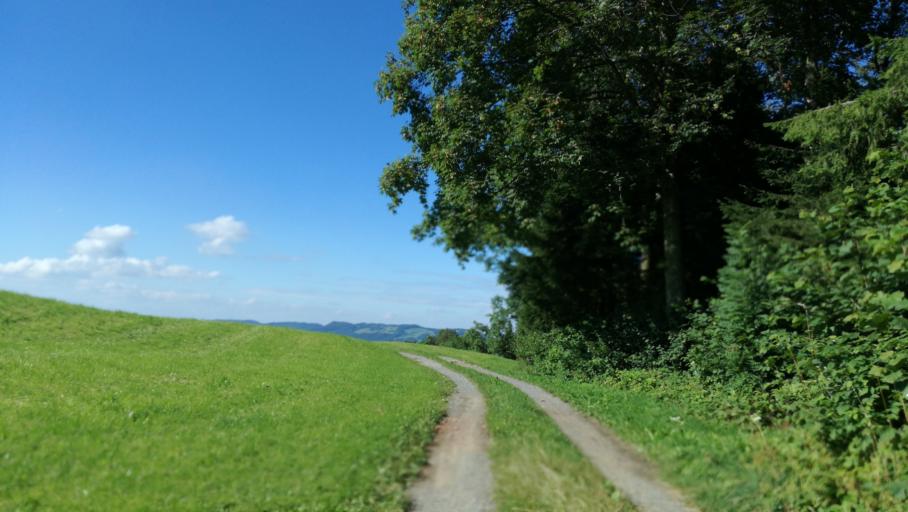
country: CH
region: Zug
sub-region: Zug
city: Unterageri
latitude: 47.1582
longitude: 8.5554
